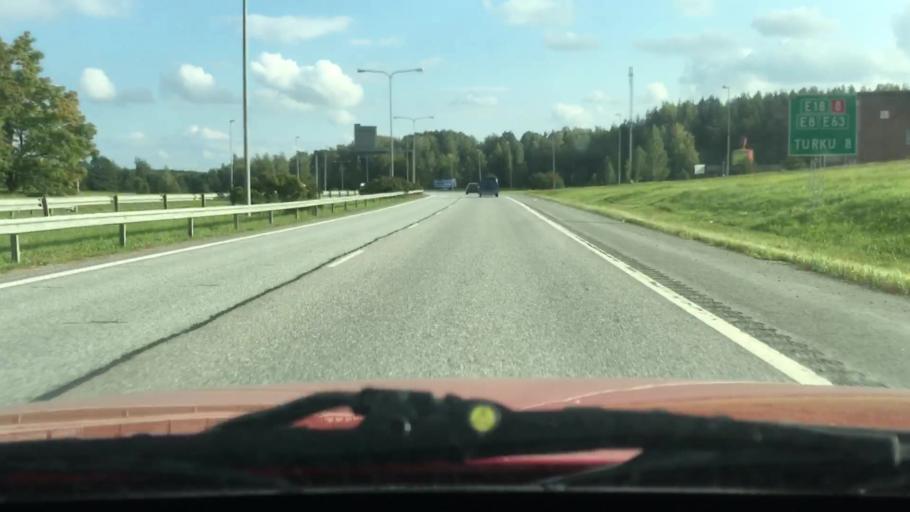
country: FI
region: Varsinais-Suomi
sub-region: Turku
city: Raisio
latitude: 60.4816
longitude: 22.1814
